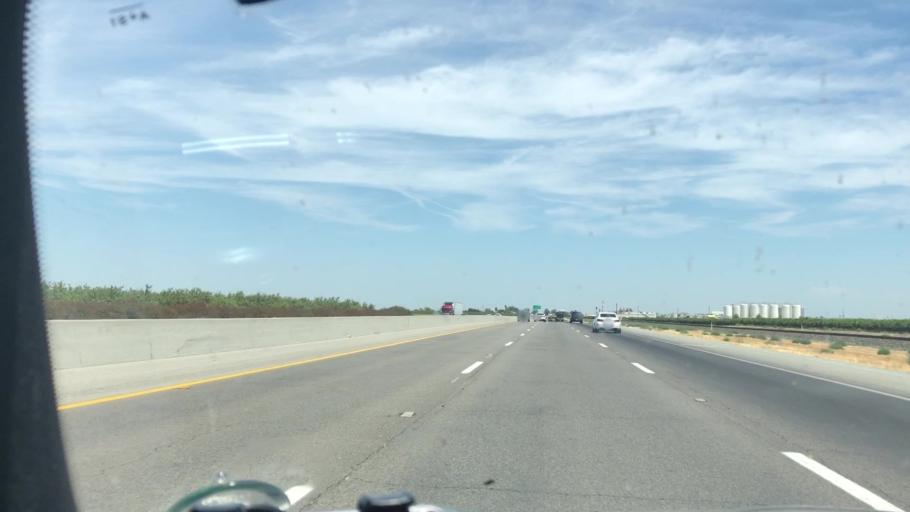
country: US
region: California
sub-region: Kern County
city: McFarland
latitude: 35.6975
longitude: -119.2312
